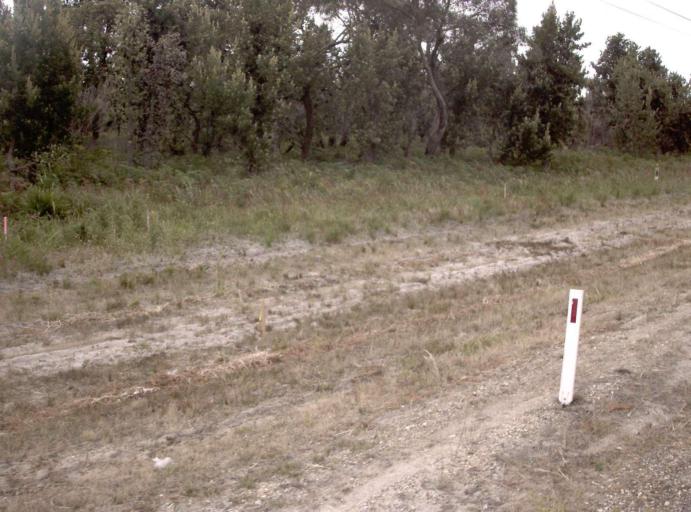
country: AU
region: Victoria
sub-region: East Gippsland
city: Bairnsdale
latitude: -38.0698
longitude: 147.5499
